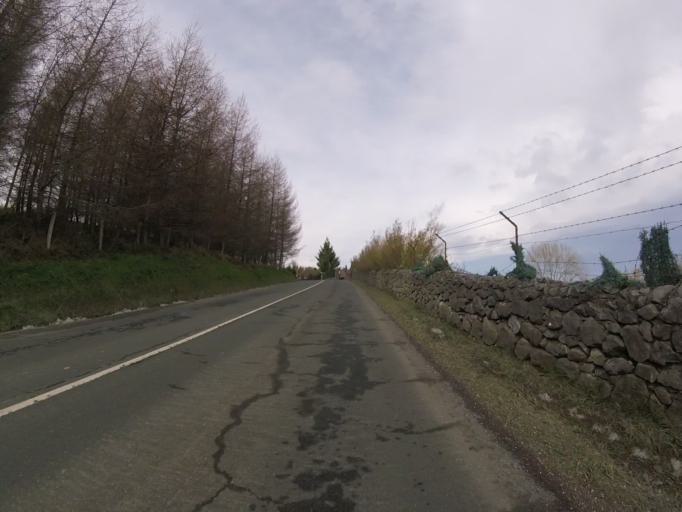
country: ES
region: Basque Country
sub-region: Provincia de Guipuzcoa
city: Errezil
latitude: 43.1506
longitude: -2.1878
